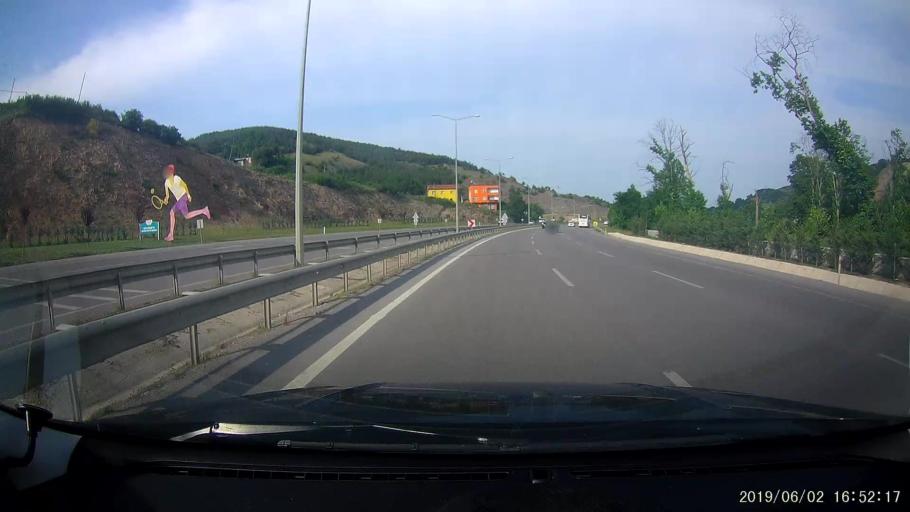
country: TR
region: Samsun
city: Samsun
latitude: 41.2857
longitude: 36.1946
